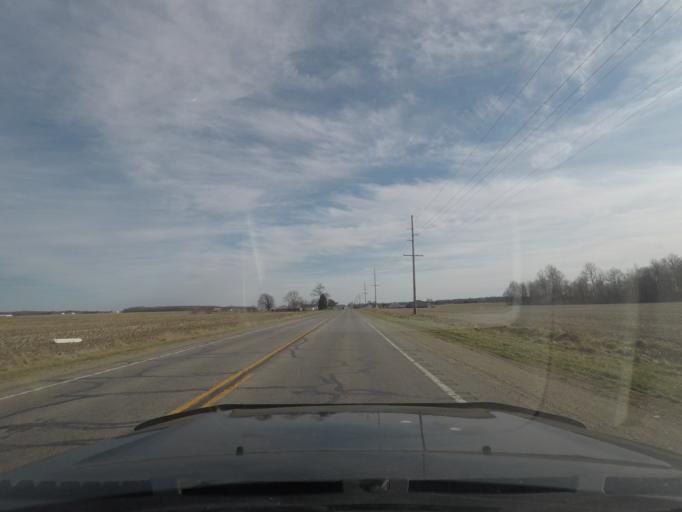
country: US
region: Indiana
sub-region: Elkhart County
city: Wakarusa
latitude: 41.5038
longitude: -86.0020
